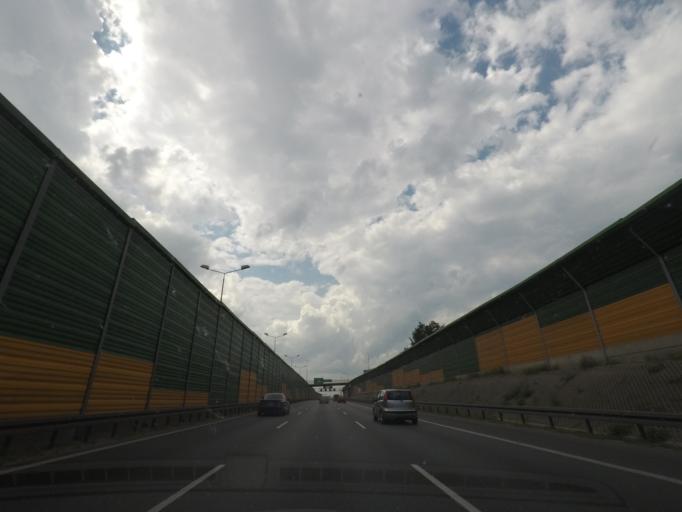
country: PL
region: Masovian Voivodeship
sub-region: Warszawa
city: Bemowo
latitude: 52.2456
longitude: 20.9120
